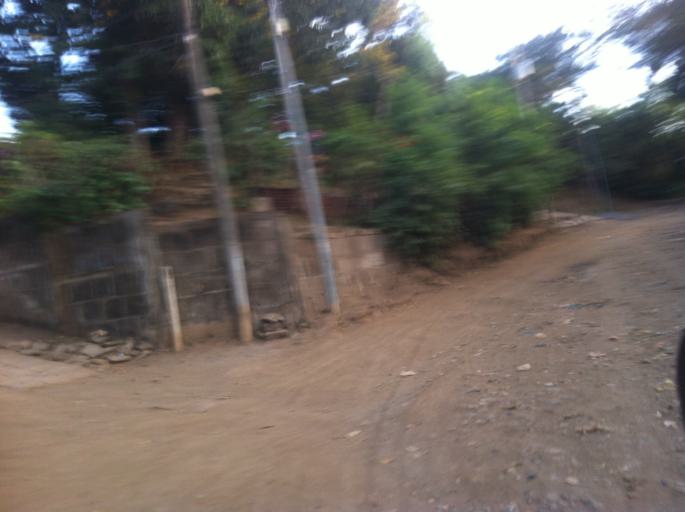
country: NI
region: Managua
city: Ciudad Sandino
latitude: 12.0990
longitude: -86.3332
